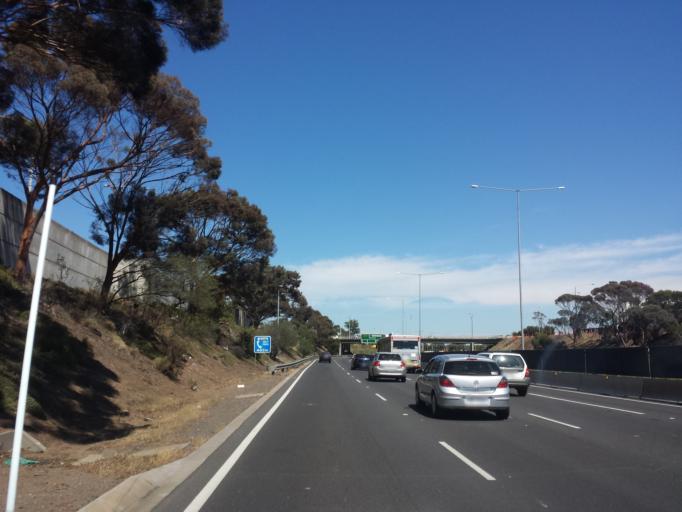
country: AU
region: Victoria
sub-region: Moonee Valley
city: Essendon North
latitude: -37.7348
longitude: 144.9075
